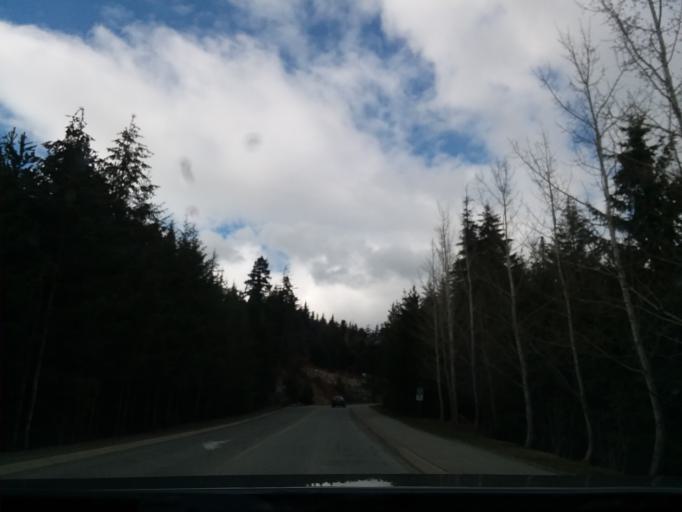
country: CA
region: British Columbia
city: Whistler
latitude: 50.1105
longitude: -122.9712
